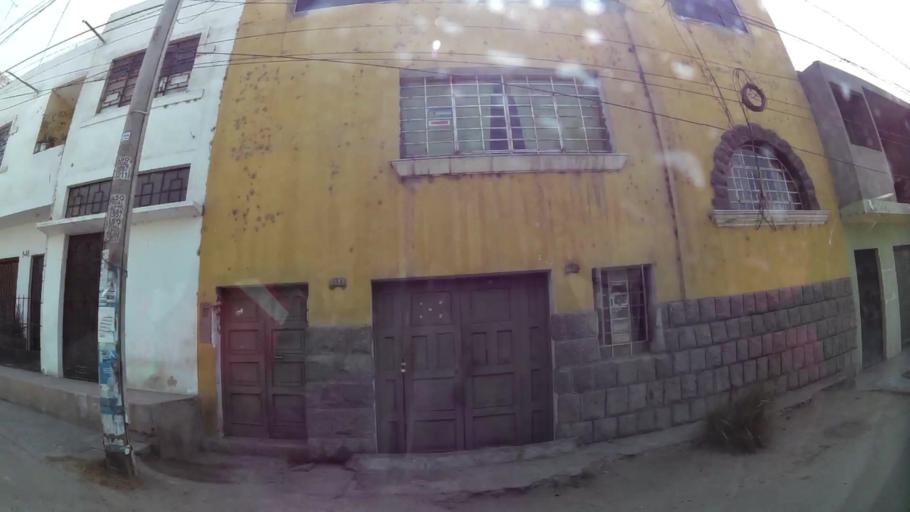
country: PE
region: Lima
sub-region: Lima
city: Asentamiento Humano Nicolas de Pierola
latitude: -11.9369
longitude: -76.7001
